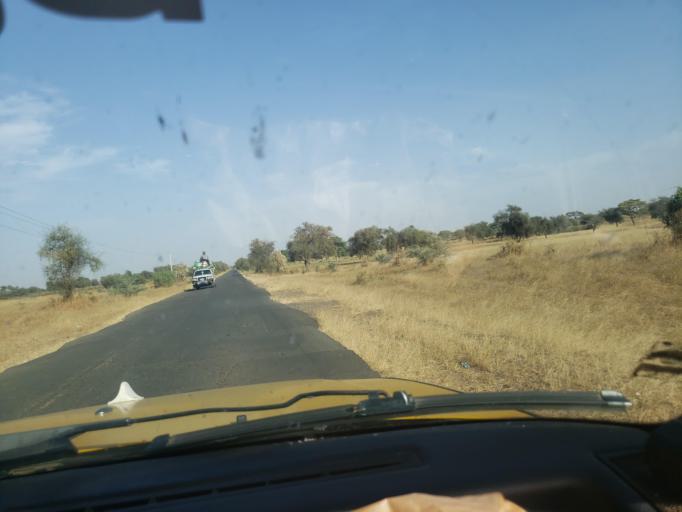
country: SN
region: Louga
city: Louga
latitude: 15.5117
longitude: -16.0066
